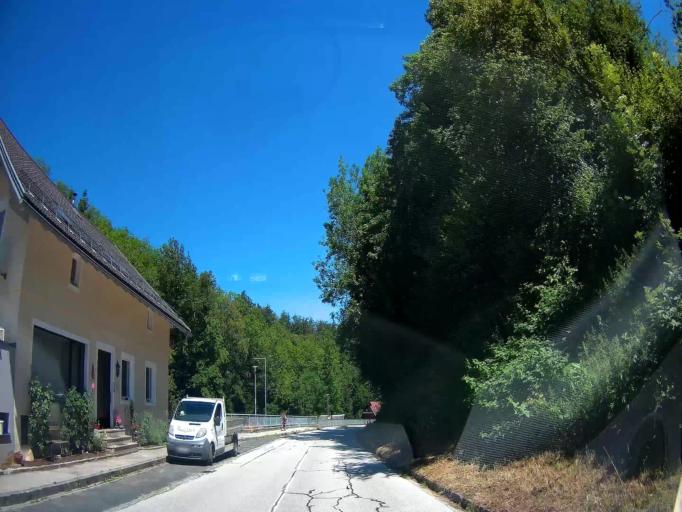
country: AT
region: Carinthia
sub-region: Politischer Bezirk Klagenfurt Land
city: Keutschach am See
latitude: 46.5930
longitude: 14.1696
